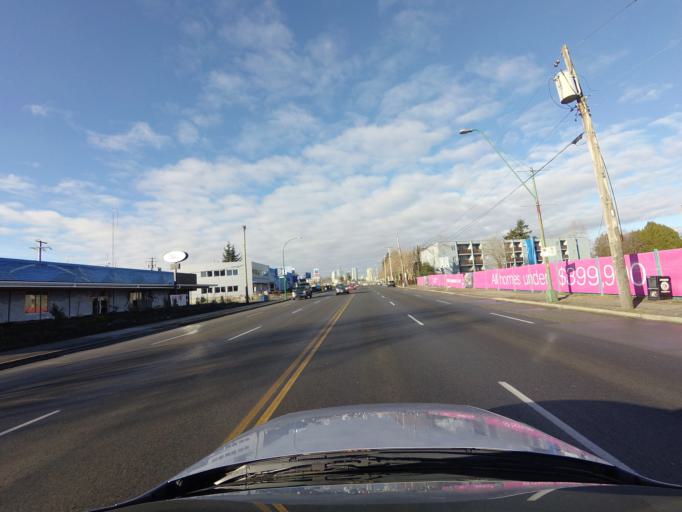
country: CA
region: British Columbia
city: Burnaby
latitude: 49.2201
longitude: -122.9728
